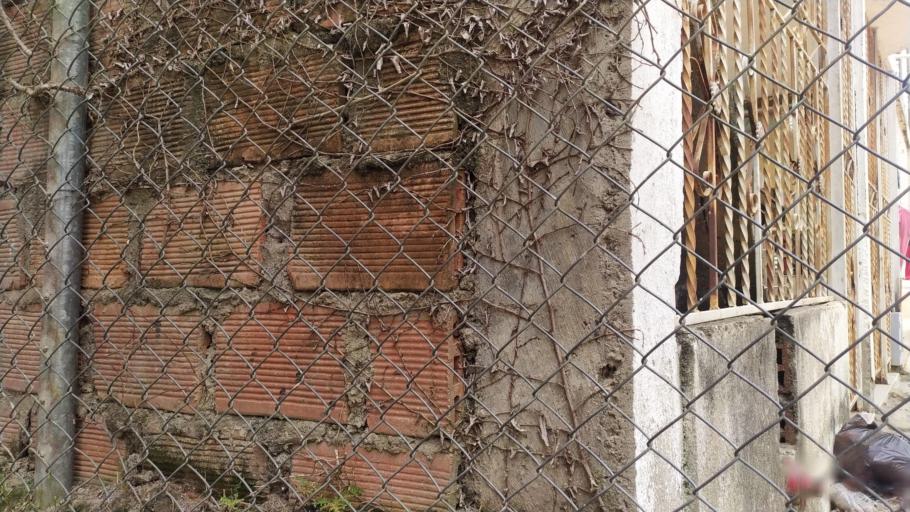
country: CO
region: Valle del Cauca
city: Jamundi
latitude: 3.2503
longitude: -76.5432
